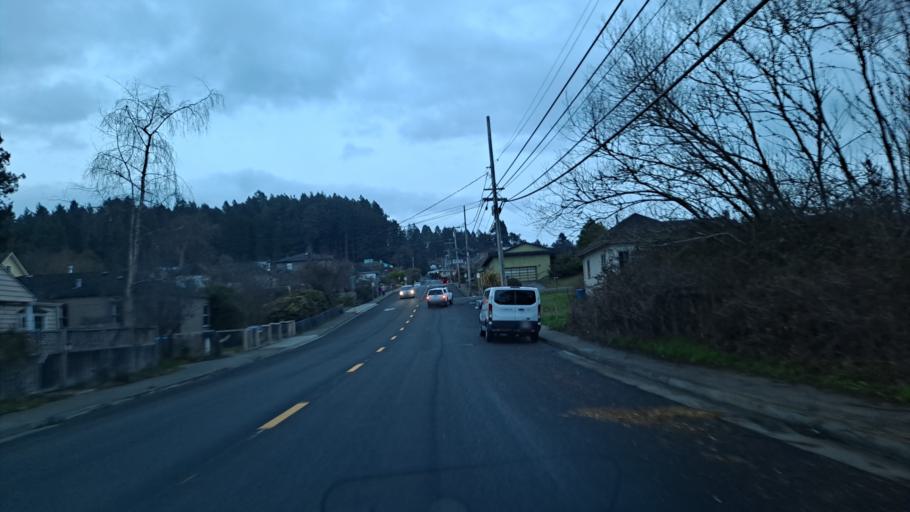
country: US
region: California
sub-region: Humboldt County
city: Arcata
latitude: 40.8692
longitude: -124.0799
